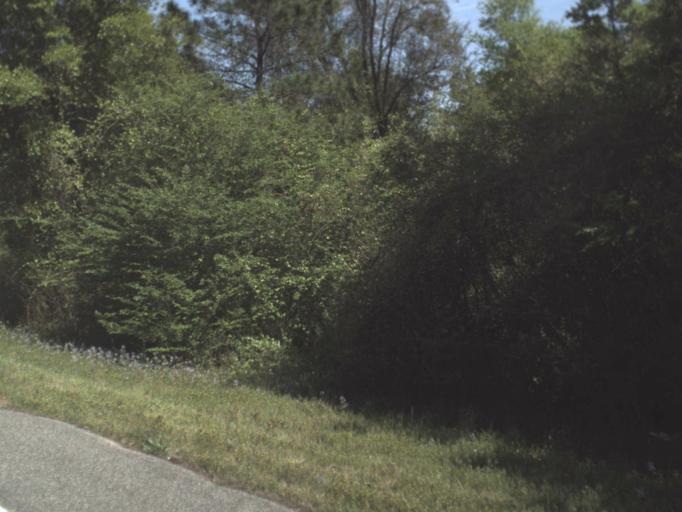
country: US
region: Florida
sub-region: Okaloosa County
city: Crestview
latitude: 30.7230
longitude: -86.7285
